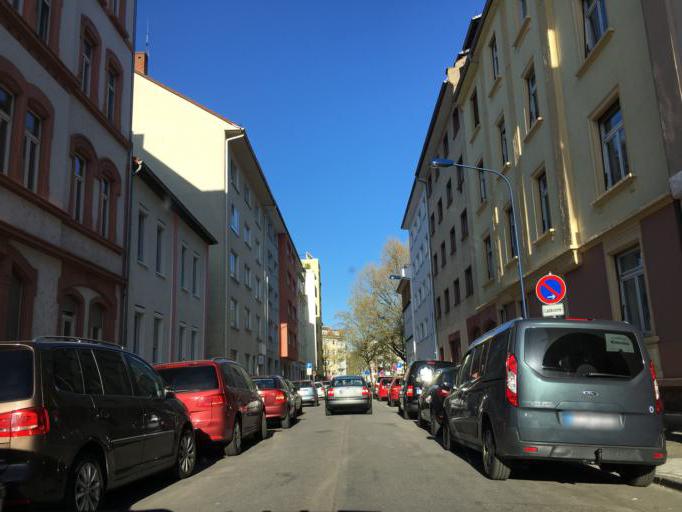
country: DE
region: Hesse
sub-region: Regierungsbezirk Darmstadt
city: Offenbach
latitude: 50.1072
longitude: 8.7493
